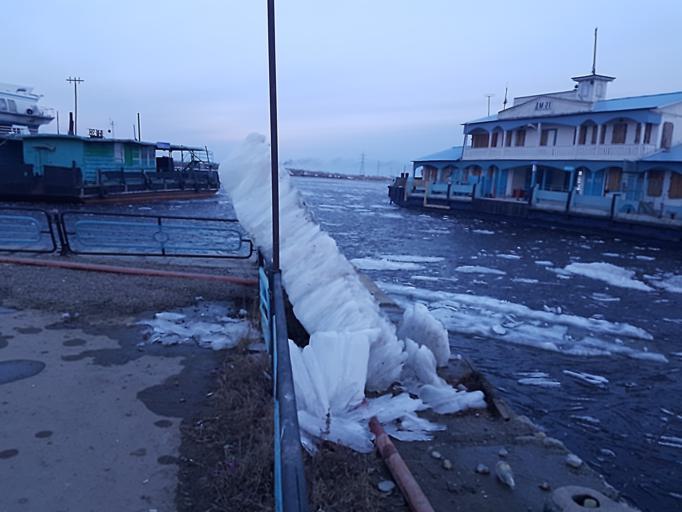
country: RU
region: Sakha
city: Yakutsk
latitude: 62.0462
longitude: 129.7704
